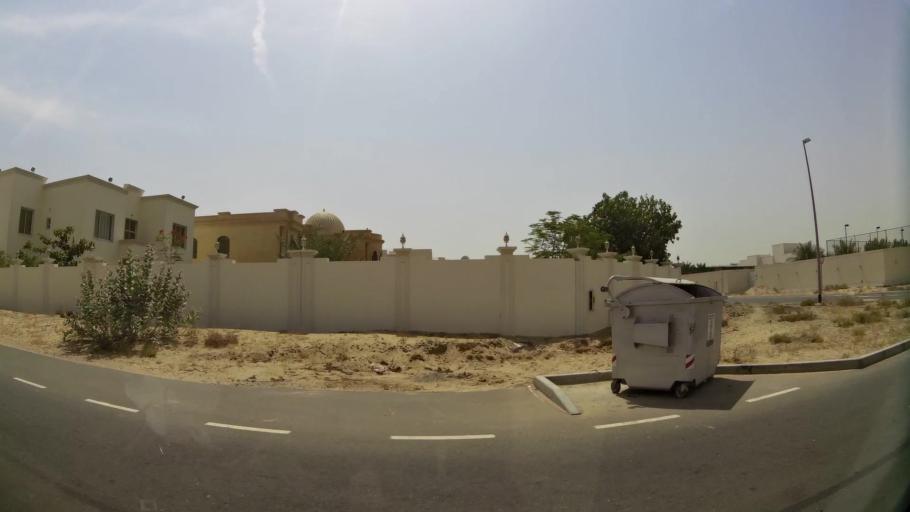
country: AE
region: Ash Shariqah
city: Sharjah
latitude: 25.2526
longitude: 55.4847
